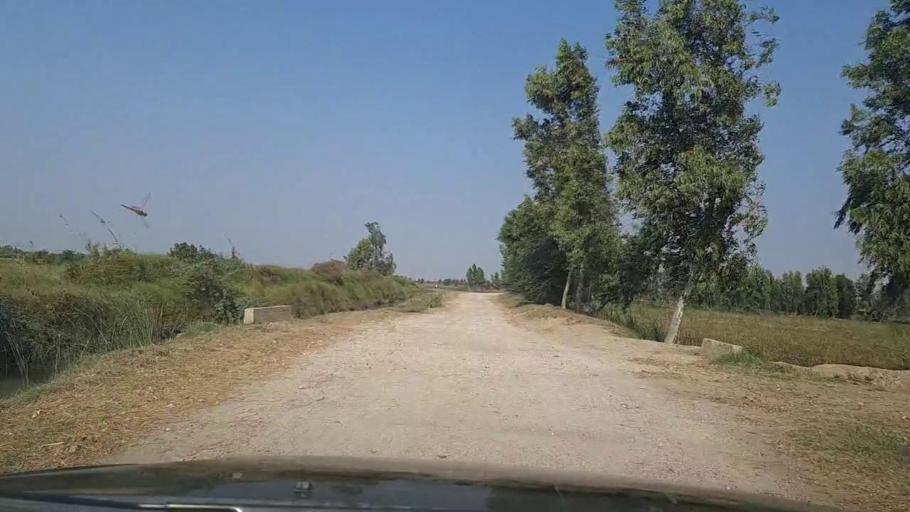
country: PK
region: Sindh
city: Thatta
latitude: 24.6222
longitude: 67.8145
